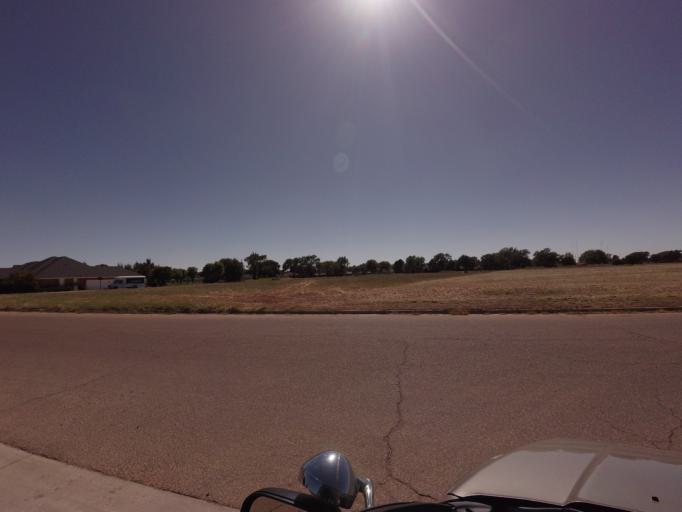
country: US
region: New Mexico
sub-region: Curry County
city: Clovis
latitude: 34.4465
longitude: -103.1904
